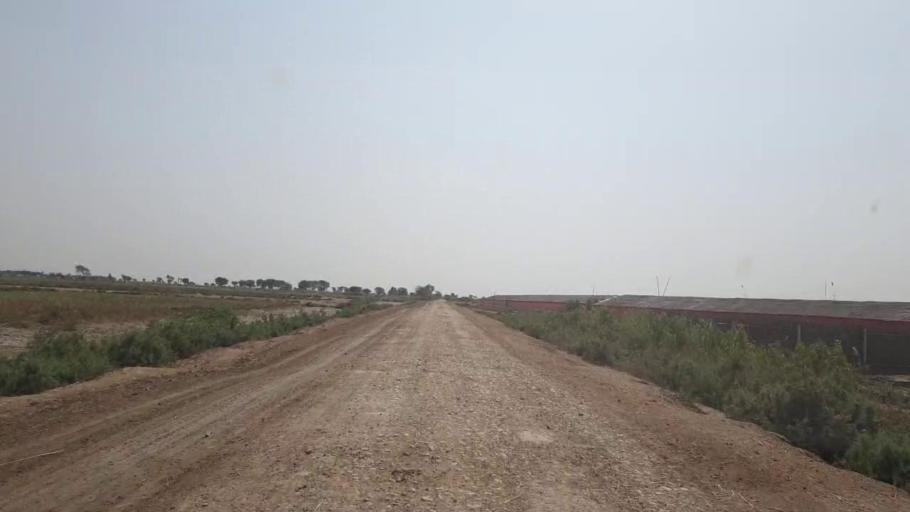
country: PK
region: Sindh
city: Jati
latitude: 24.4247
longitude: 68.5524
